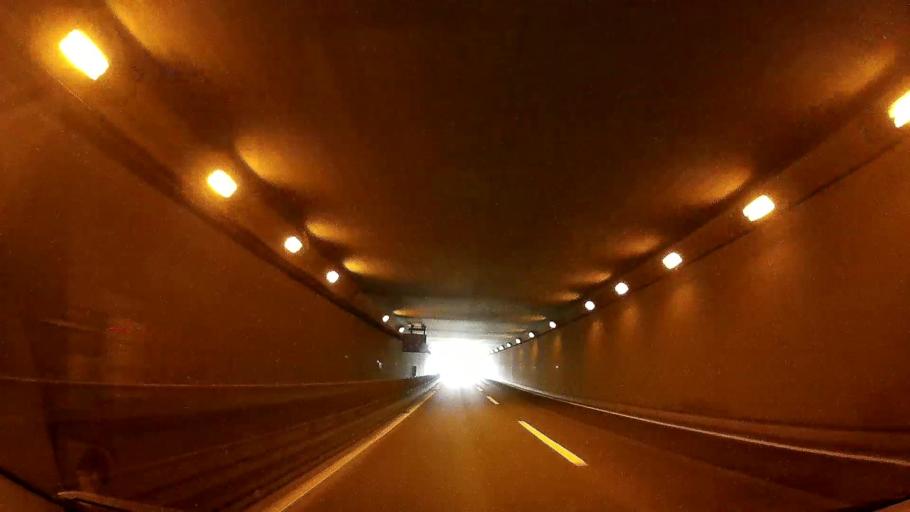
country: JP
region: Hokkaido
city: Chitose
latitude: 42.7916
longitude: 141.6769
